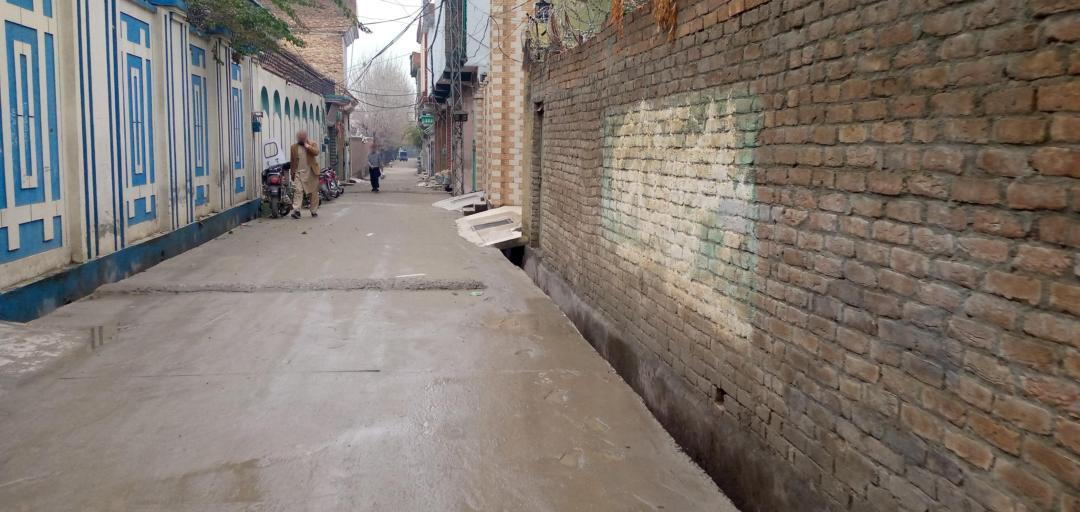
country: PK
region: Khyber Pakhtunkhwa
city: Mingora
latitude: 34.7791
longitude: 72.3537
